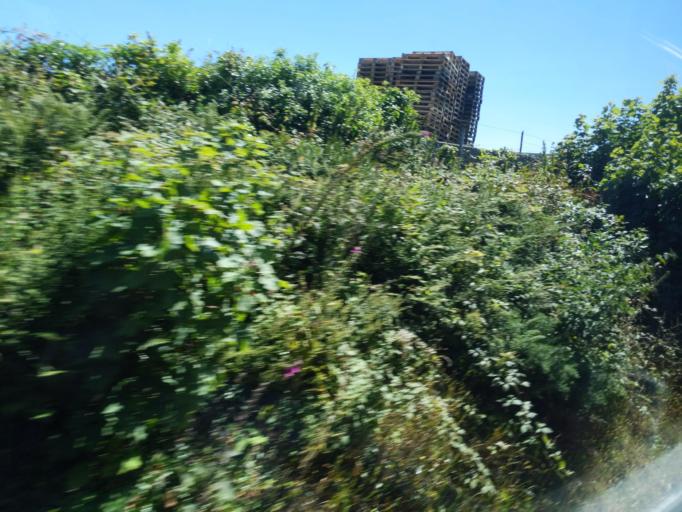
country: GB
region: England
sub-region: Cornwall
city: Redruth
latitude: 50.2464
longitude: -5.2204
